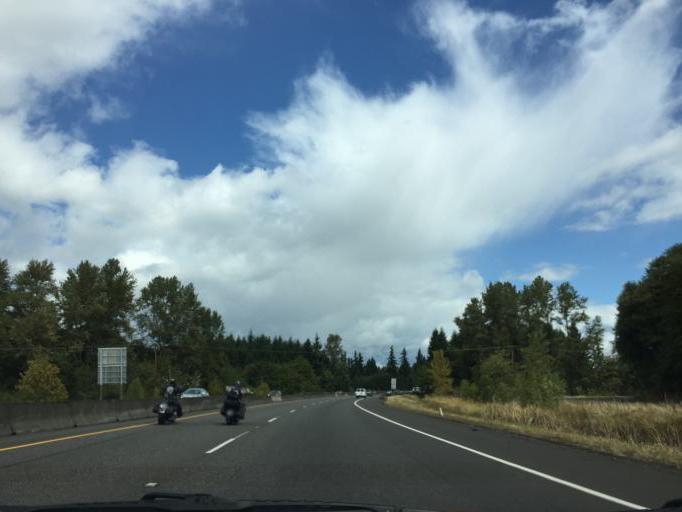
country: US
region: Washington
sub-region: Lewis County
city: Winlock
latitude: 46.3971
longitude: -122.9001
